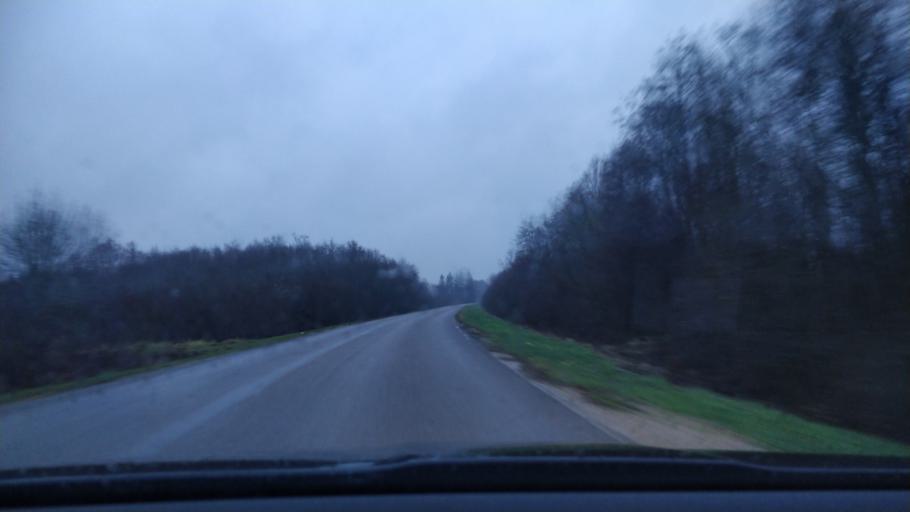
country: EE
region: Laeaene
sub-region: Lihula vald
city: Lihula
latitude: 58.7036
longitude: 23.8611
